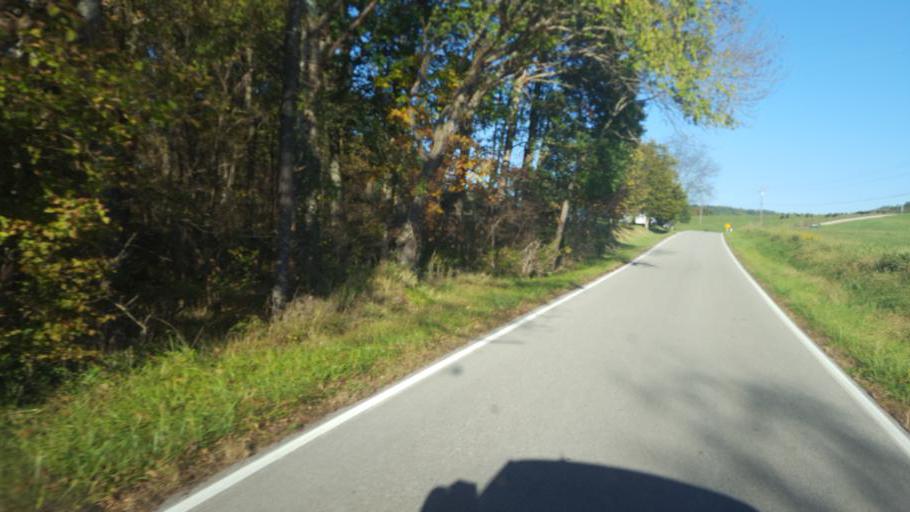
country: US
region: Kentucky
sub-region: Fleming County
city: Flemingsburg
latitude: 38.4962
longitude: -83.5613
